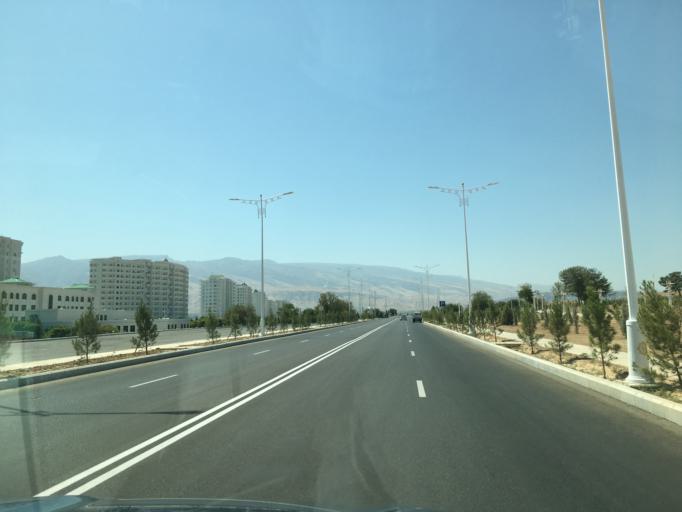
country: TM
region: Ahal
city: Ashgabat
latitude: 37.9232
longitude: 58.3547
